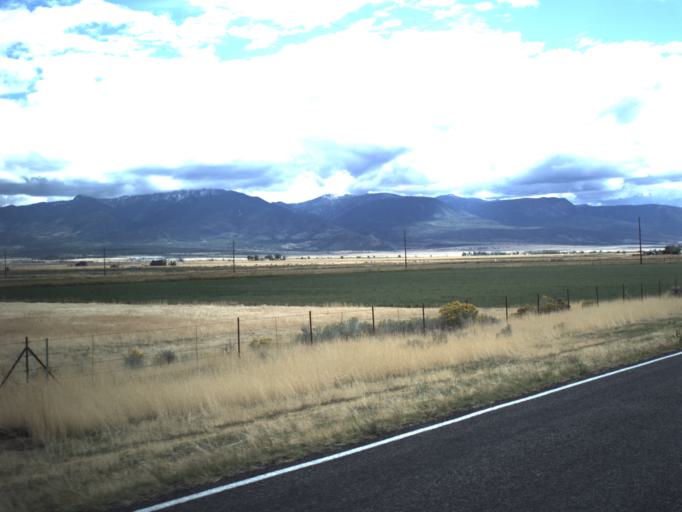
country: US
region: Utah
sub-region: Millard County
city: Fillmore
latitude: 38.9822
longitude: -112.4099
